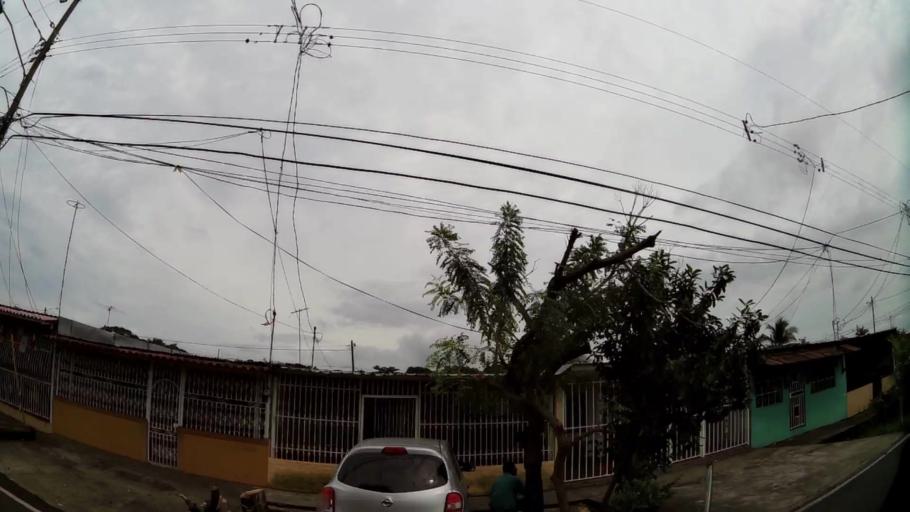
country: PA
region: Panama
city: San Miguelito
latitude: 9.0512
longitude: -79.4320
